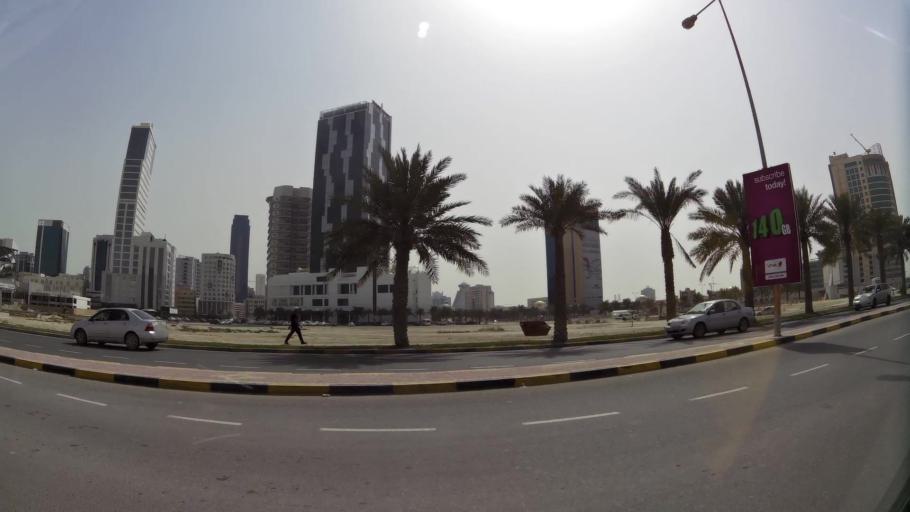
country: BH
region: Manama
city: Jidd Hafs
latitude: 26.2359
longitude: 50.5342
